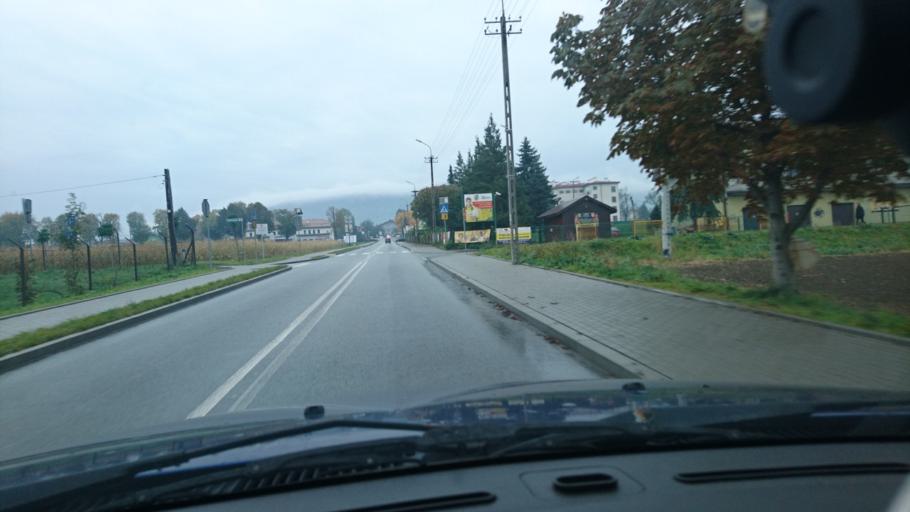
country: PL
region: Silesian Voivodeship
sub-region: Powiat bielski
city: Kozy
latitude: 49.8491
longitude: 19.1453
